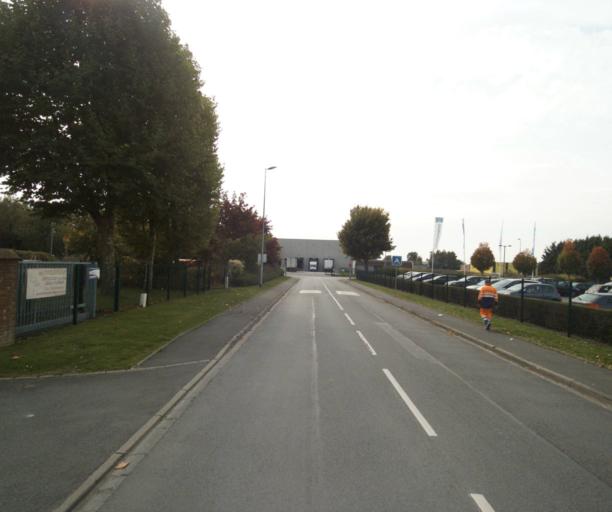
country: FR
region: Nord-Pas-de-Calais
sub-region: Departement du Nord
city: Vendeville
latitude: 50.5650
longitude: 3.0684
